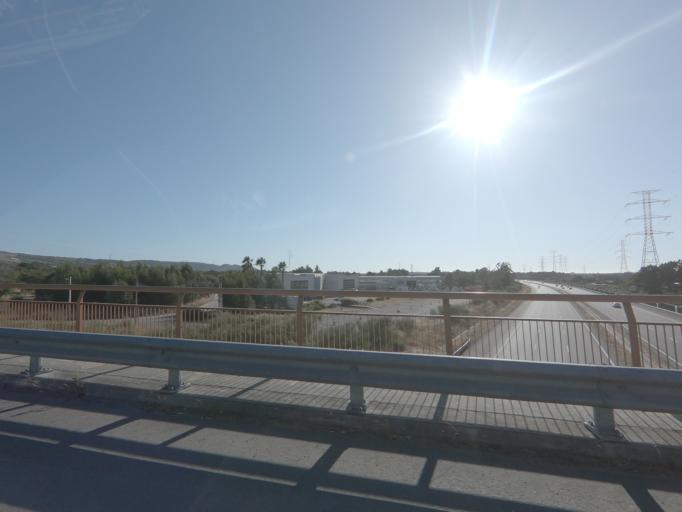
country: PT
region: Setubal
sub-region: Palmela
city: Palmela
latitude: 38.5854
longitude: -8.9163
